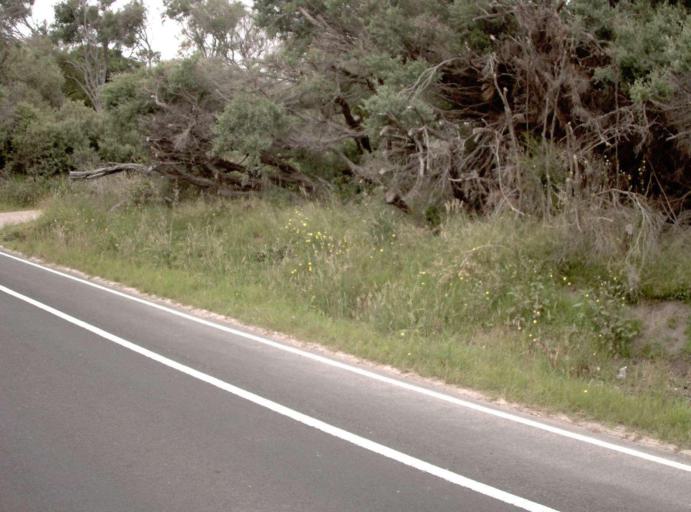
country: AU
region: Victoria
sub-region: Mornington Peninsula
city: Mount Martha
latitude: -38.2597
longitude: 145.0353
